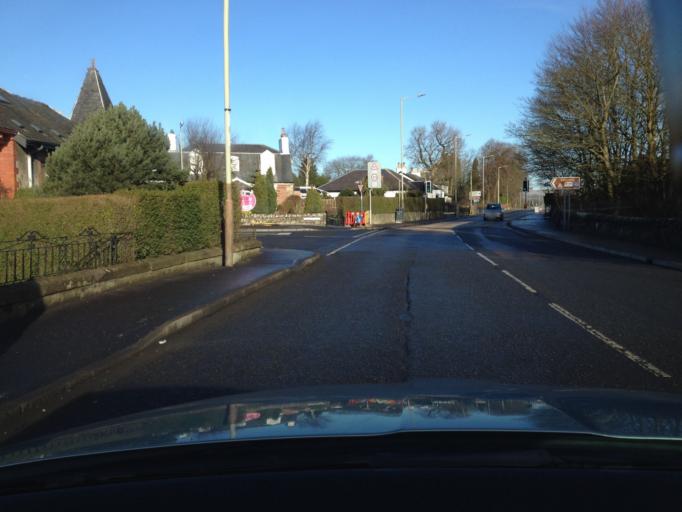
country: GB
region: Scotland
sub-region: Perth and Kinross
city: Kinross
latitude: 56.2141
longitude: -3.4270
